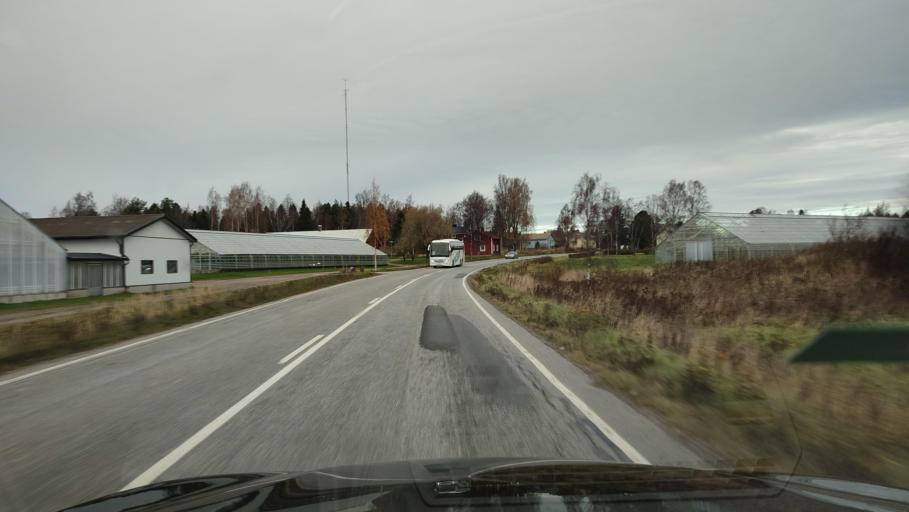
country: FI
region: Ostrobothnia
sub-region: Sydosterbotten
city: Naerpes
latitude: 62.4054
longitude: 21.3513
